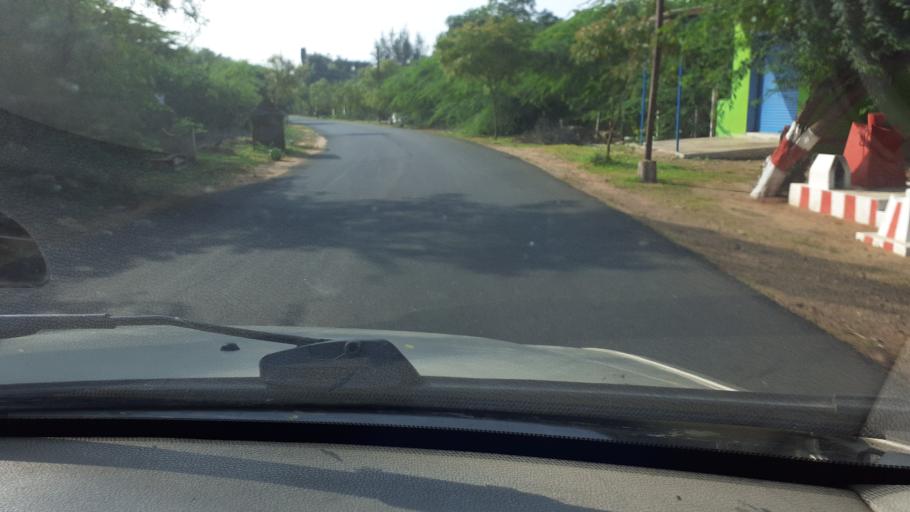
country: IN
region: Tamil Nadu
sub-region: Thoothukkudi
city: Eral
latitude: 8.5786
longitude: 78.0259
